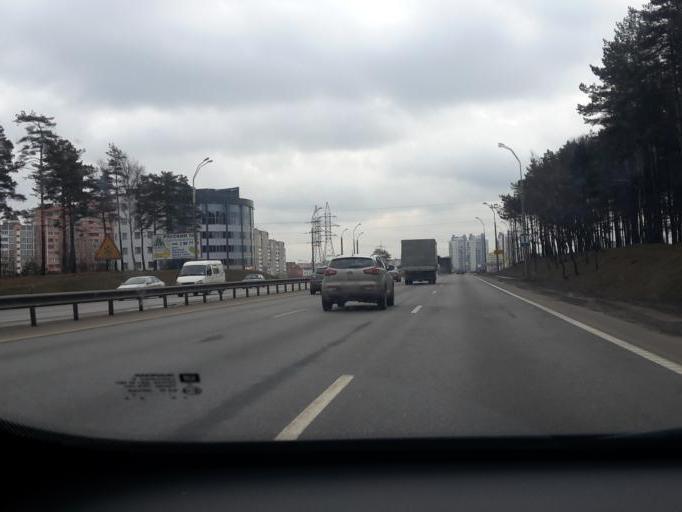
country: BY
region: Minsk
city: Borovlyany
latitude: 53.9471
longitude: 27.6621
